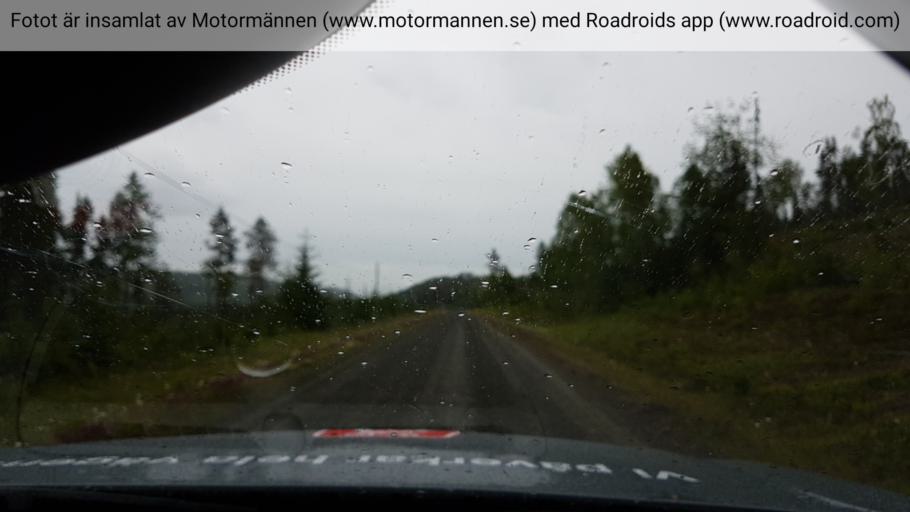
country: SE
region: Jaemtland
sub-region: Bergs Kommun
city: Hoverberg
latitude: 62.5400
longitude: 14.7005
